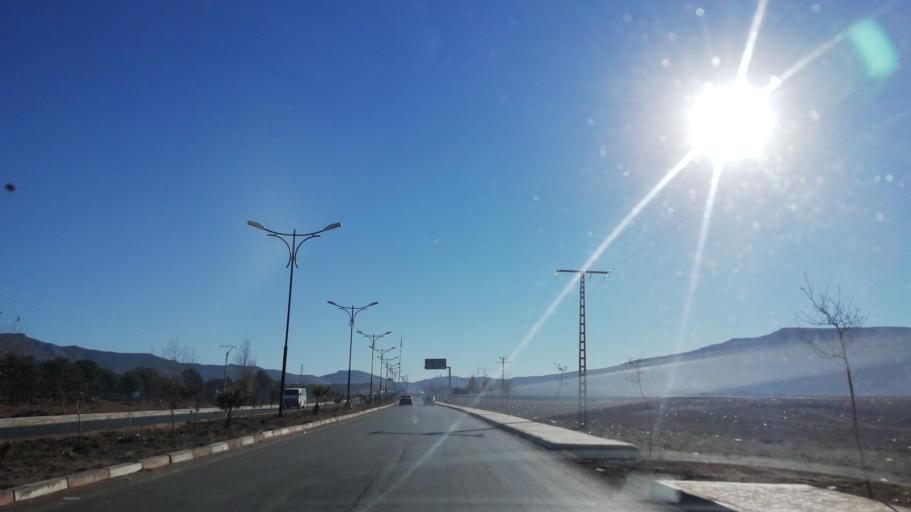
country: DZ
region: El Bayadh
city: El Bayadh
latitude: 33.6624
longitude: 1.0538
